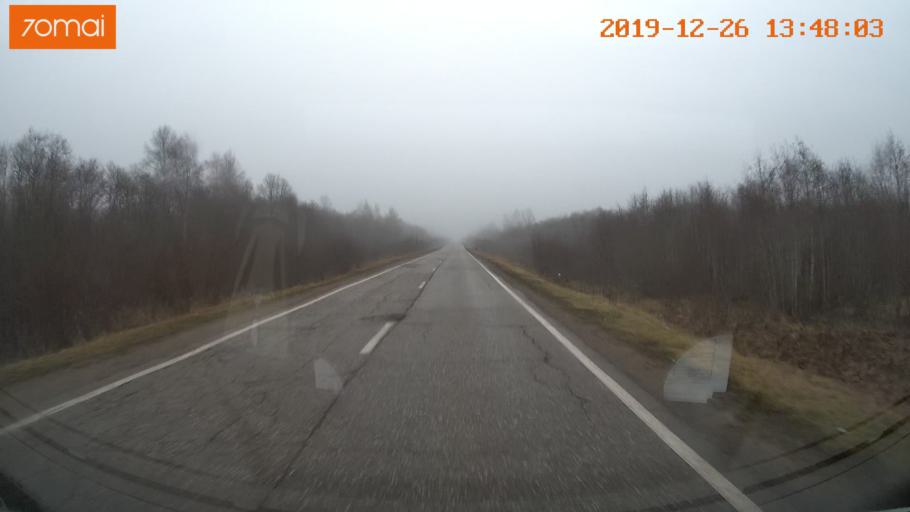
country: RU
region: Vologda
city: Sheksna
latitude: 58.6796
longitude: 38.5424
